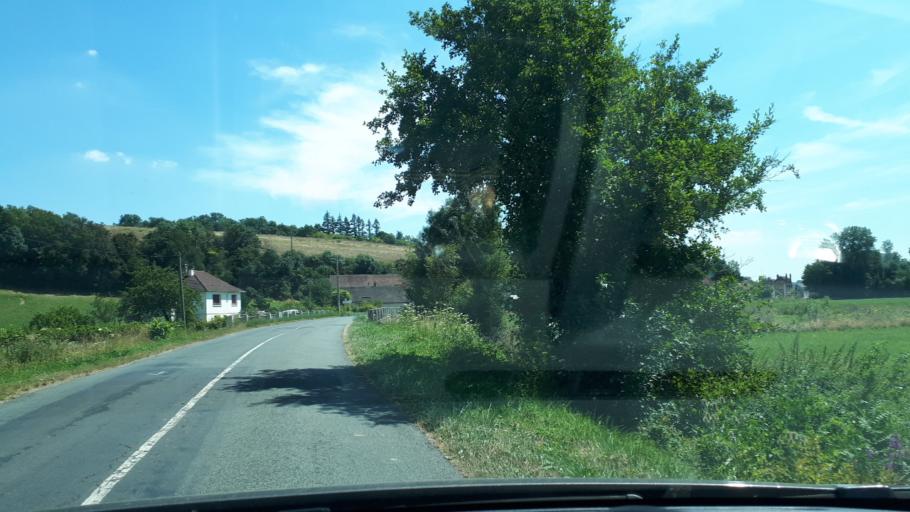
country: FR
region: Centre
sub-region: Departement du Loir-et-Cher
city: Villiers-sur-Loir
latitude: 47.8146
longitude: 0.9592
